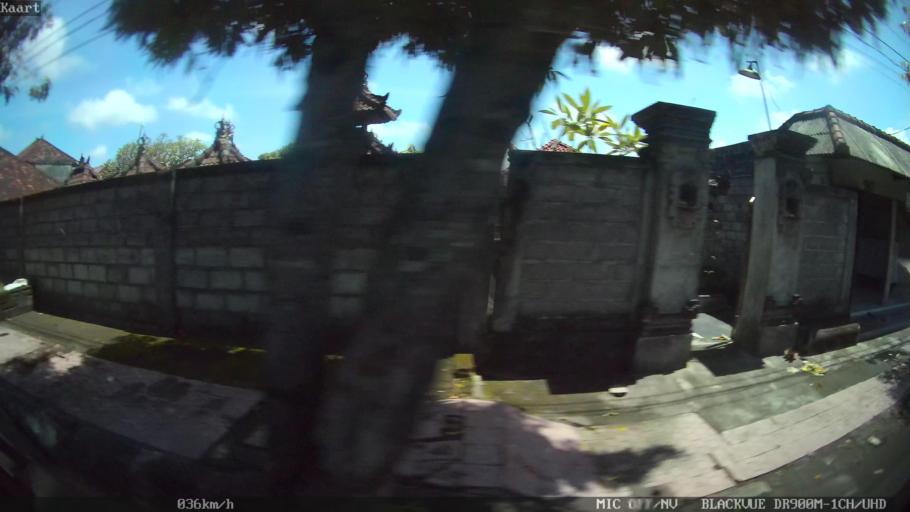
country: ID
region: Bali
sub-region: Kabupaten Gianyar
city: Ubud
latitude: -8.5553
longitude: 115.3148
